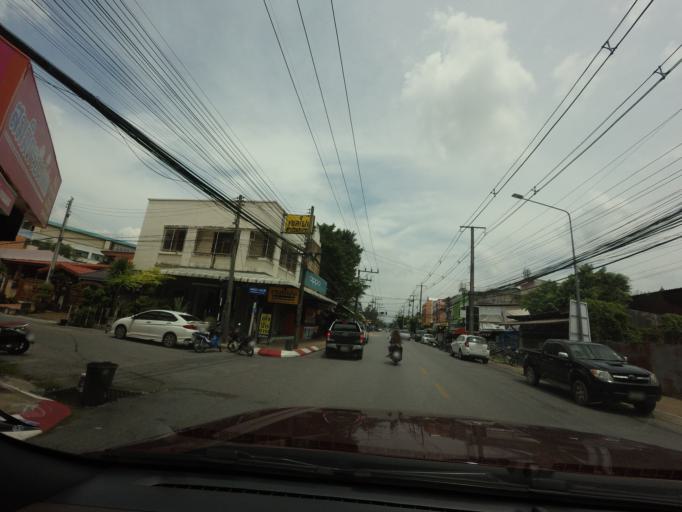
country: TH
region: Yala
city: Yala
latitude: 6.5487
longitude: 101.2933
